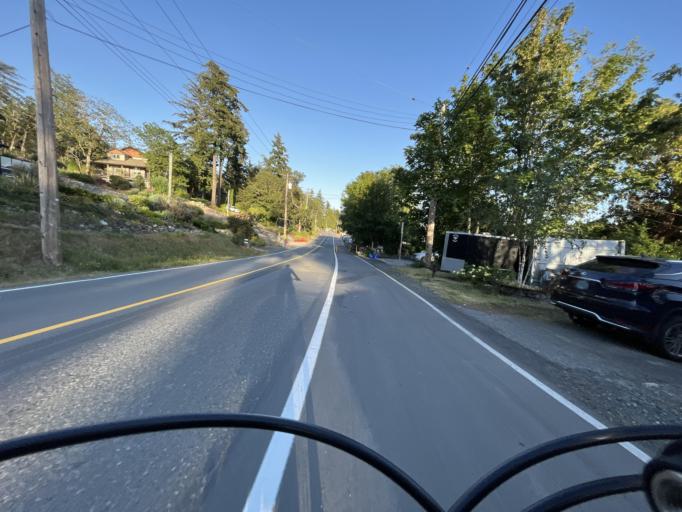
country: CA
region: British Columbia
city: Langford
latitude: 48.4506
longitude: -123.5270
